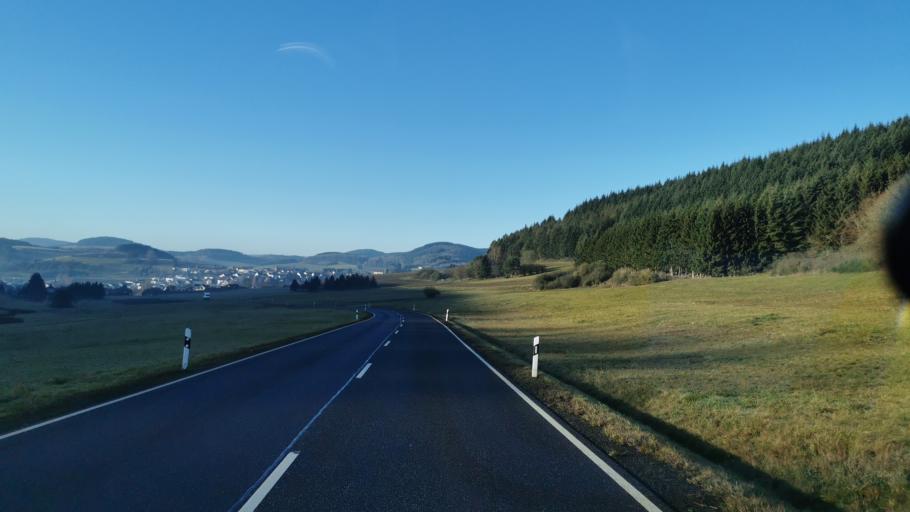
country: DE
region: Rheinland-Pfalz
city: Oberstadtfeld
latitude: 50.1819
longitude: 6.7812
